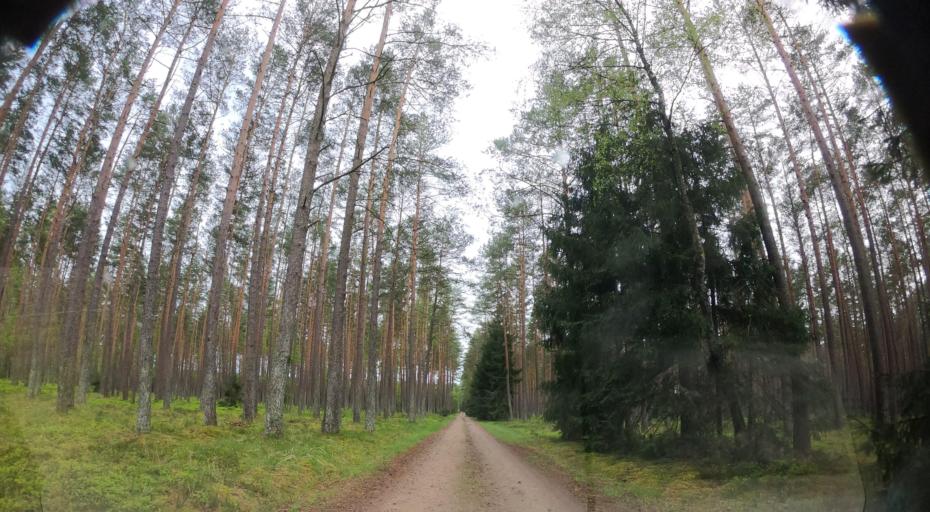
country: PL
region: West Pomeranian Voivodeship
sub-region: Powiat koszalinski
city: Bobolice
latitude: 54.0664
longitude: 16.4358
